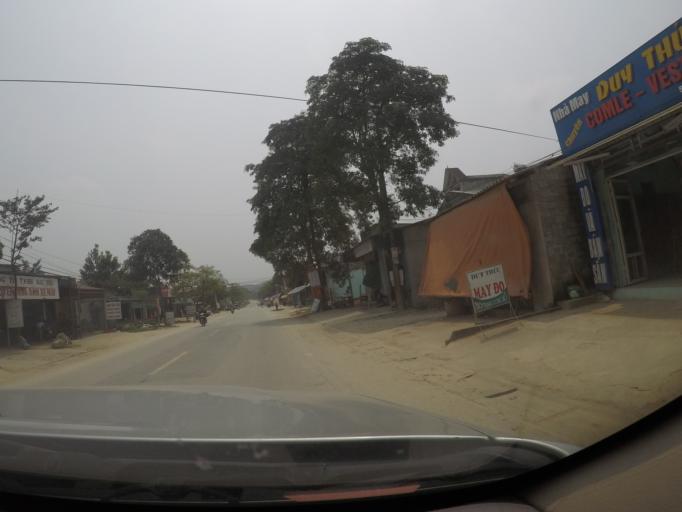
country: VN
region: Thanh Hoa
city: Thi Tran Thuong Xuan
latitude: 19.8094
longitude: 105.3951
